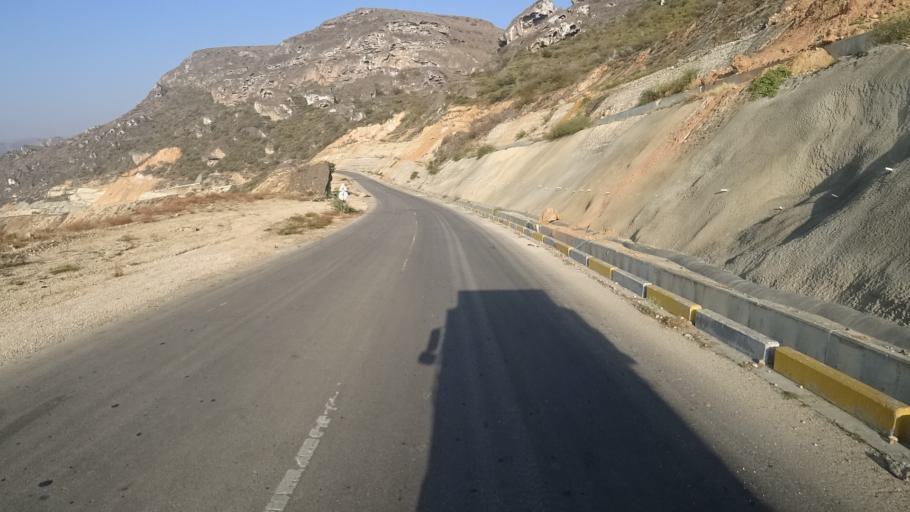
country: YE
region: Al Mahrah
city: Hawf
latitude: 16.7566
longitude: 53.2275
